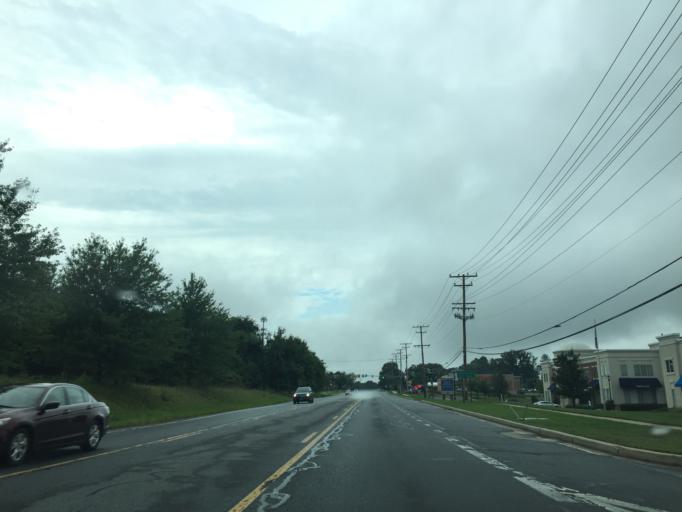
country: US
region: Maryland
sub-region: Harford County
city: Bel Air South
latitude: 39.5009
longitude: -76.3261
